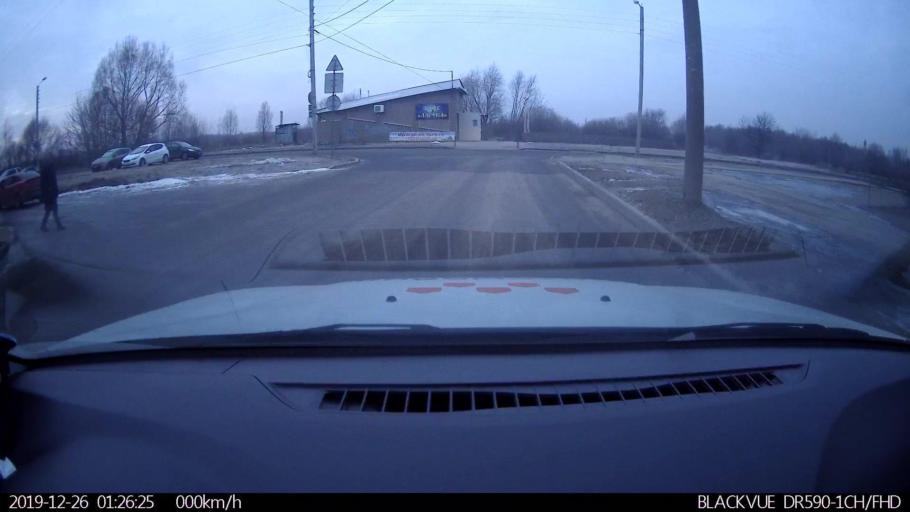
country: RU
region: Nizjnij Novgorod
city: Gorbatovka
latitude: 56.2661
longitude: 43.8651
